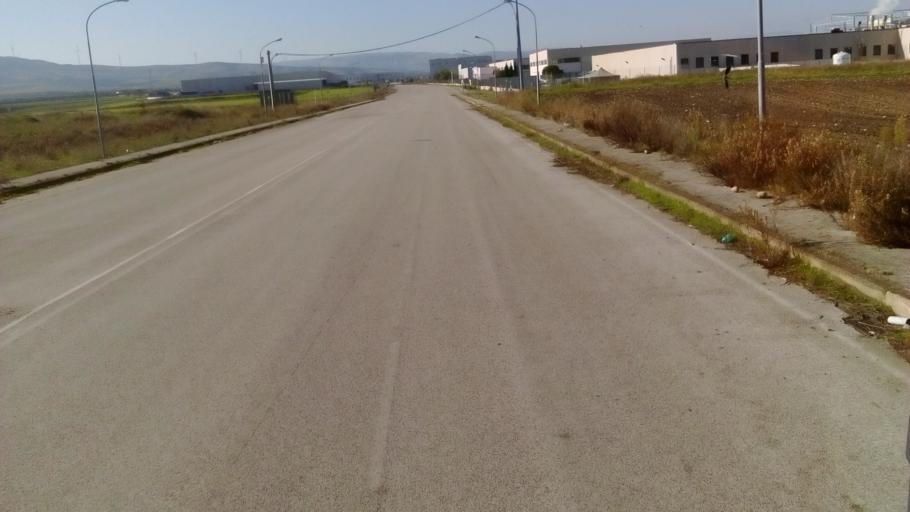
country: IT
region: Basilicate
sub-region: Provincia di Potenza
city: Melfi
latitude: 41.0779
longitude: 15.6681
